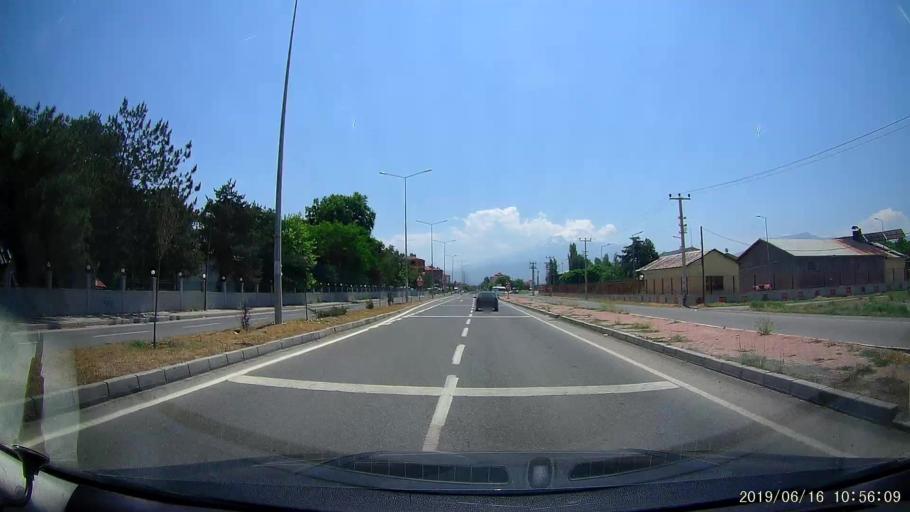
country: TR
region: Igdir
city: Igdir
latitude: 39.9318
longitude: 44.0187
